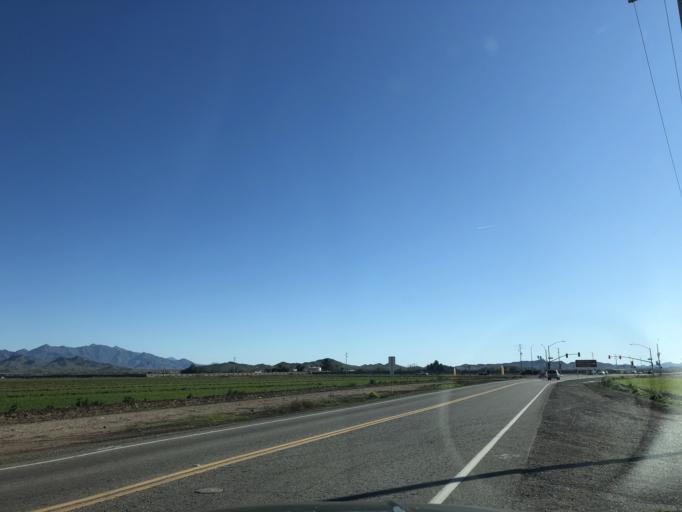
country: US
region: Arizona
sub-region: Maricopa County
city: Buckeye
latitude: 33.3795
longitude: -112.4782
